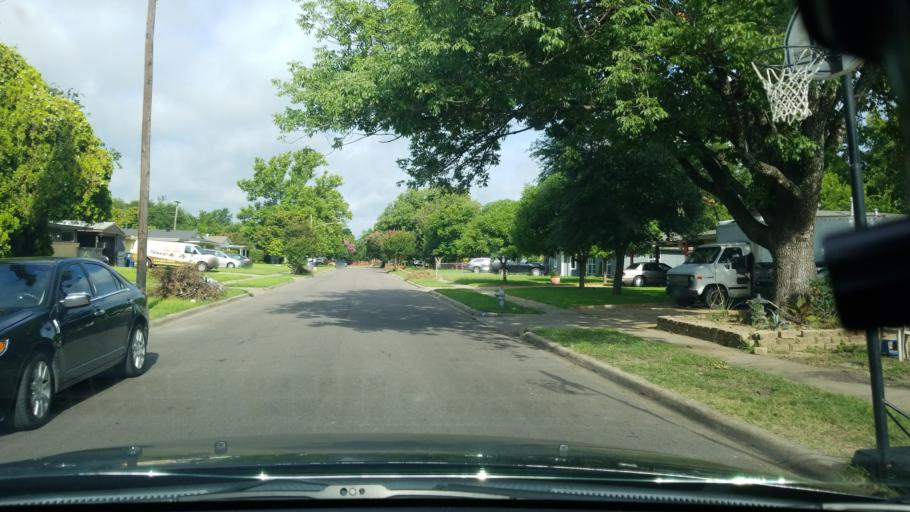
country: US
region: Texas
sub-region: Dallas County
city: Mesquite
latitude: 32.8206
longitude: -96.6718
